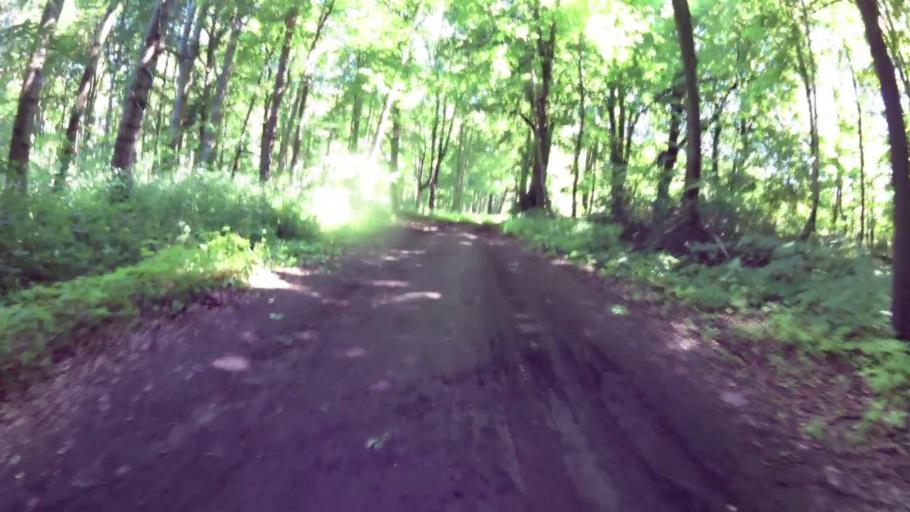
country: PL
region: West Pomeranian Voivodeship
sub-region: Powiat kamienski
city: Dziwnow
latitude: 54.0370
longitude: 14.8238
